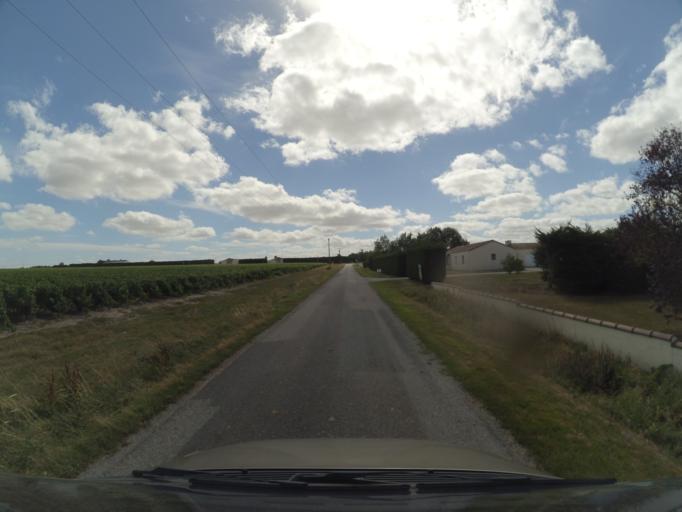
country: FR
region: Pays de la Loire
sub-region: Departement de la Loire-Atlantique
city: Remouille
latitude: 47.0505
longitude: -1.3918
